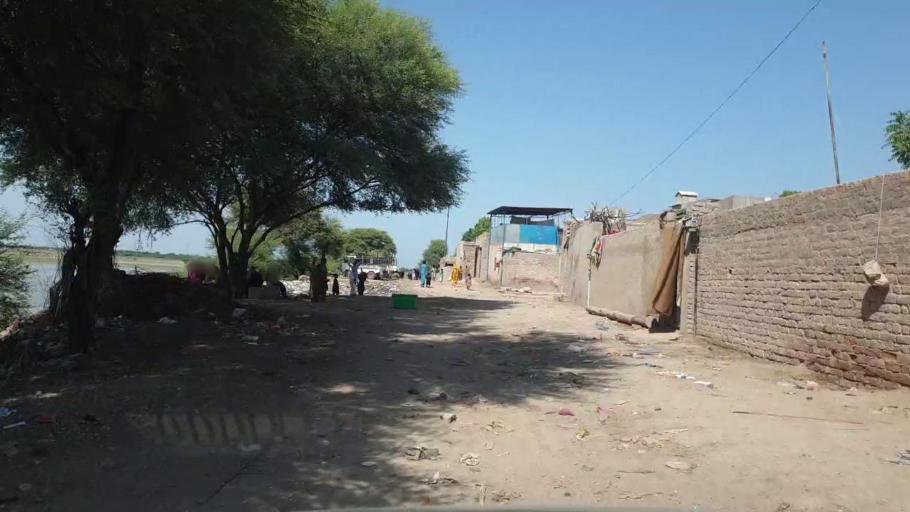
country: PK
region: Sindh
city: Matiari
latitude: 25.6487
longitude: 68.4945
